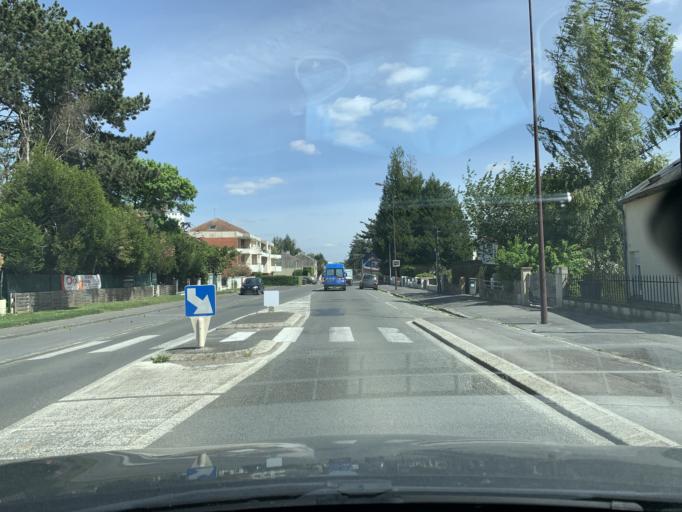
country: FR
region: Picardie
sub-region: Departement de l'Aisne
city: Saint-Quentin
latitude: 49.8583
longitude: 3.2992
